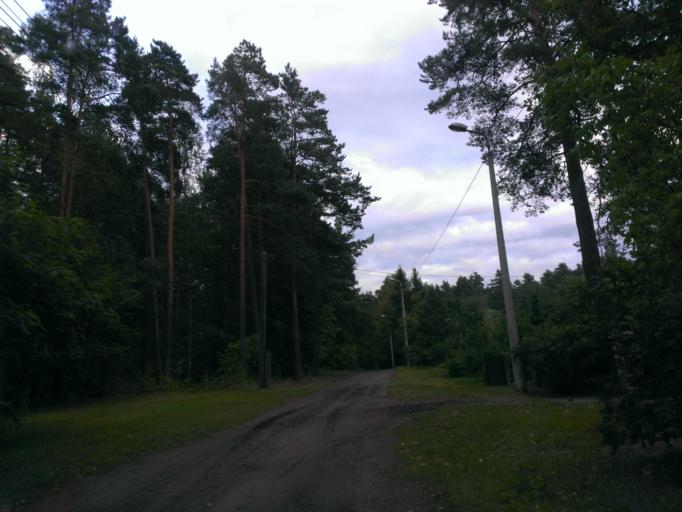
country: LV
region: Riga
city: Bergi
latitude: 56.9843
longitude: 24.3067
